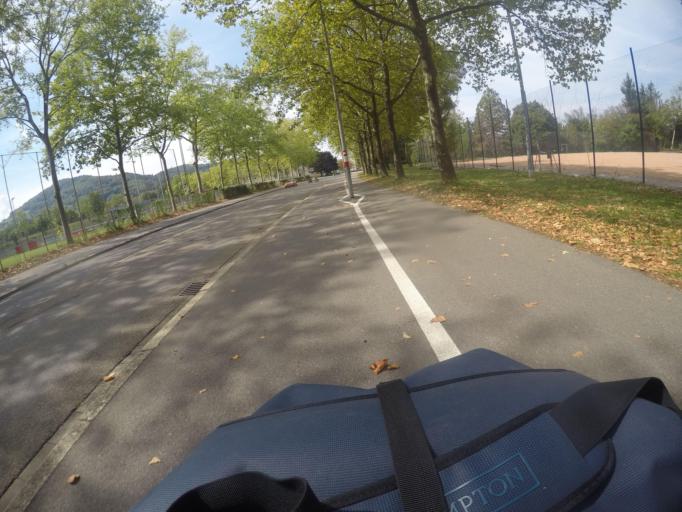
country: DE
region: Baden-Wuerttemberg
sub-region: Freiburg Region
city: Merzhausen
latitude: 47.9788
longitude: 7.8182
